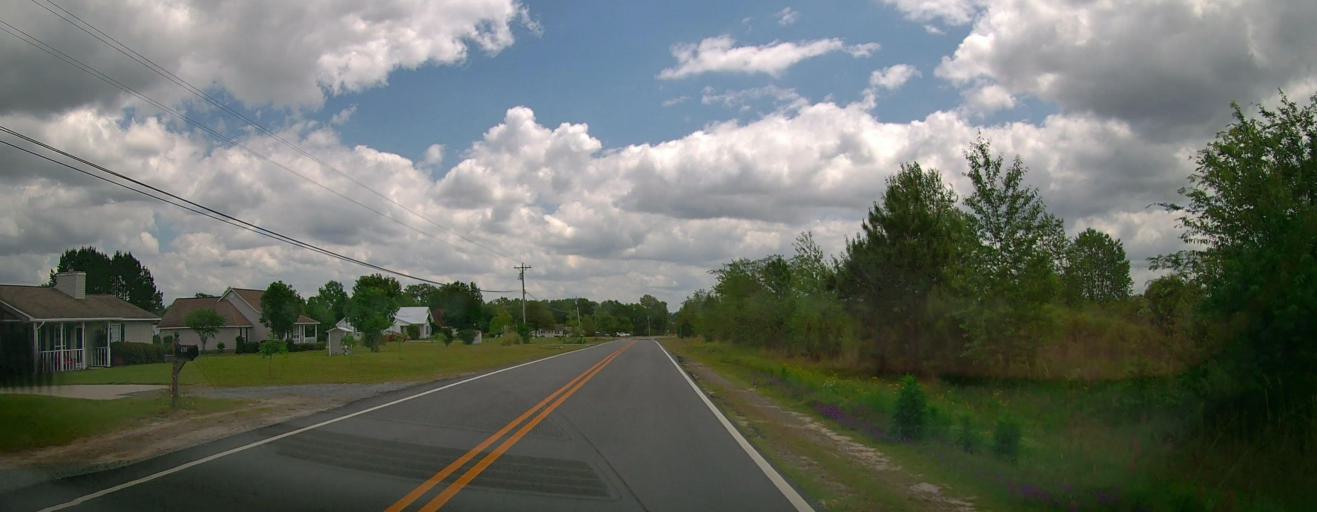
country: US
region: Georgia
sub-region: Laurens County
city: Dublin
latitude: 32.6003
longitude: -82.9631
